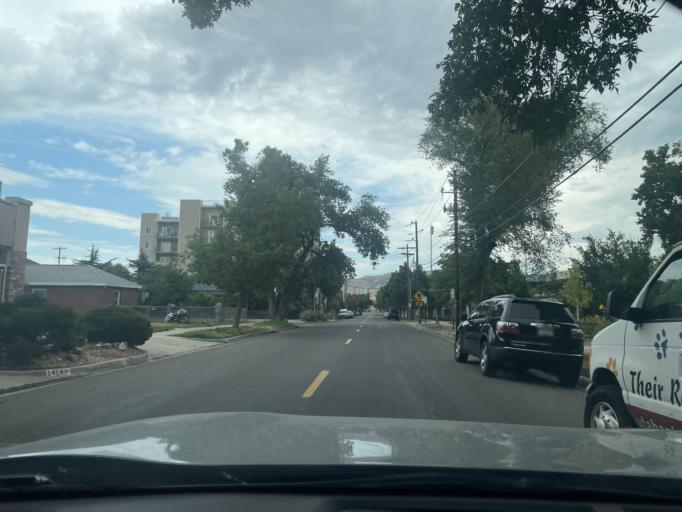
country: US
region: Utah
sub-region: Salt Lake County
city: South Salt Lake
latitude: 40.7387
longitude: -111.8939
